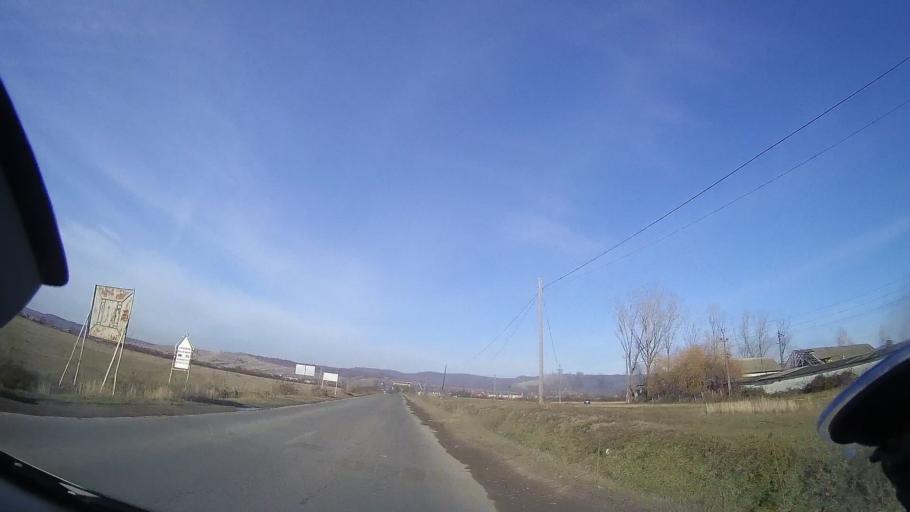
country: RO
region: Bihor
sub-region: Comuna Astileu
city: Astileu
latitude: 47.0386
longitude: 22.3915
